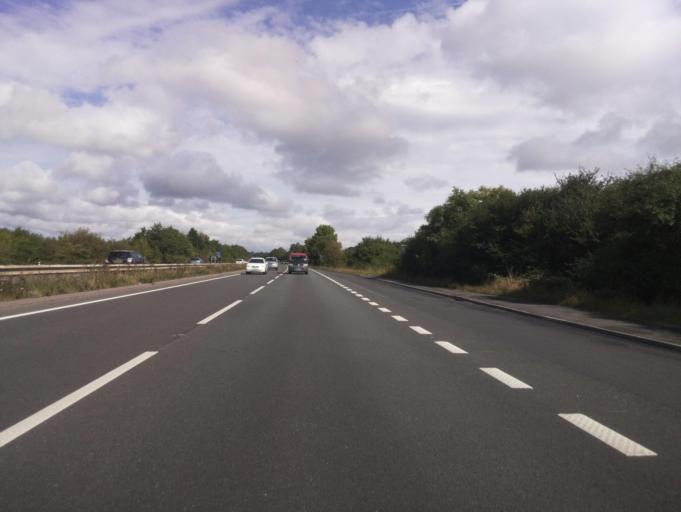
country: GB
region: England
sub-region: Derbyshire
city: Heage
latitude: 53.0361
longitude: -1.4361
